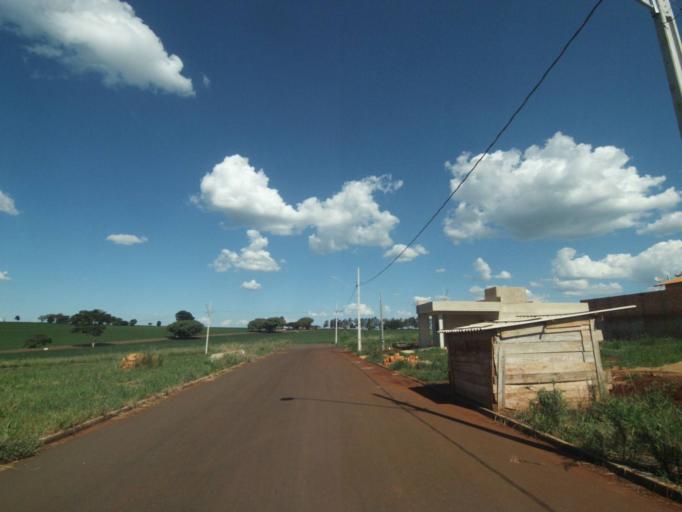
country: BR
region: Parana
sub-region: Sertanopolis
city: Sertanopolis
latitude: -23.0357
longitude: -50.8104
